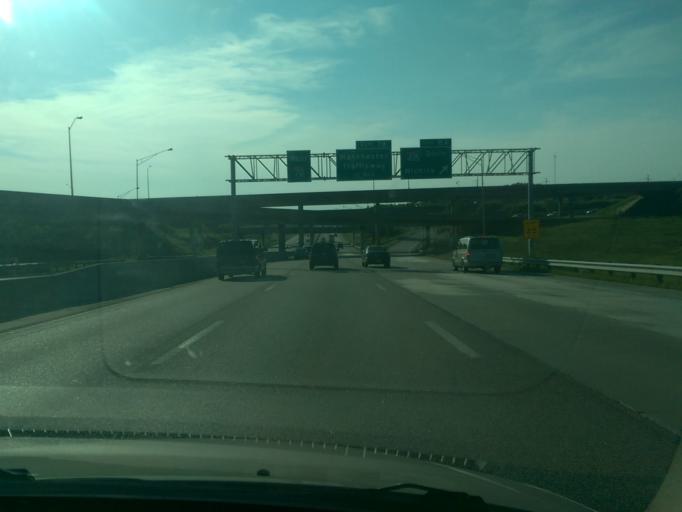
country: US
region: Missouri
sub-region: Jackson County
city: Raytown
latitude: 39.0581
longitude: -94.4877
